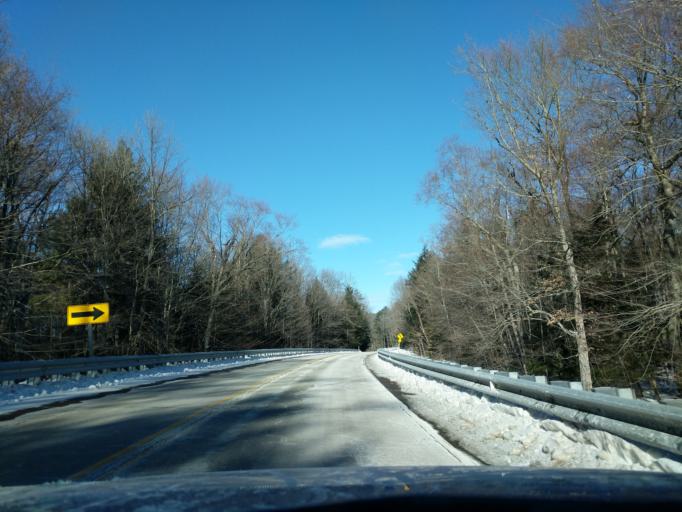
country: US
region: Wisconsin
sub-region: Menominee County
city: Keshena
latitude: 45.0998
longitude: -88.6344
